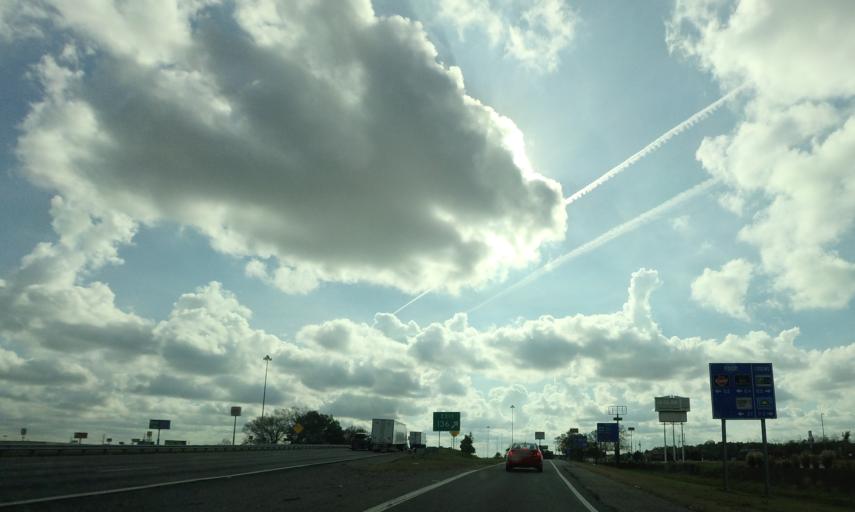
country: US
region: Georgia
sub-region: Houston County
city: Perry
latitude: 32.4744
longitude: -83.7433
